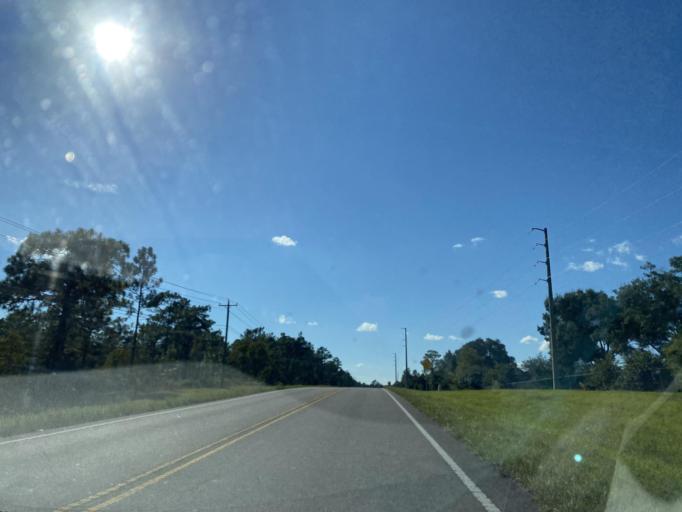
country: US
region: Florida
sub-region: Marion County
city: Ocala
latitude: 29.0521
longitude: -82.2671
